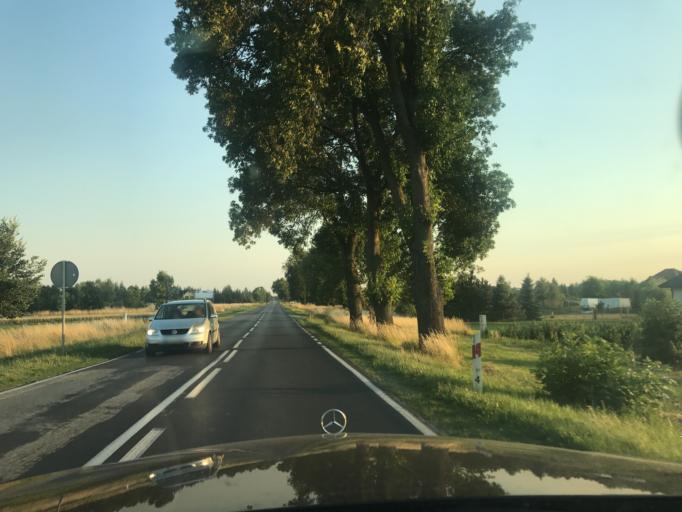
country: PL
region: Lublin Voivodeship
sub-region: Powiat lubartowski
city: Lubartow
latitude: 51.4928
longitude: 22.6339
